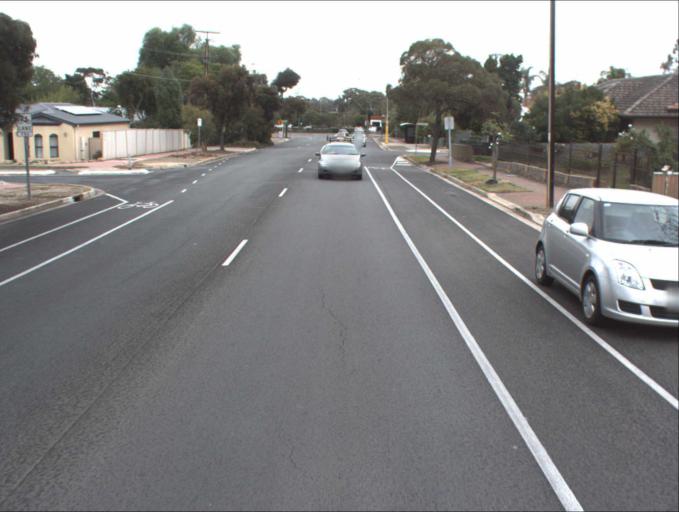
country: AU
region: South Australia
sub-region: Port Adelaide Enfield
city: Gilles Plains
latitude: -34.8578
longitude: 138.6597
